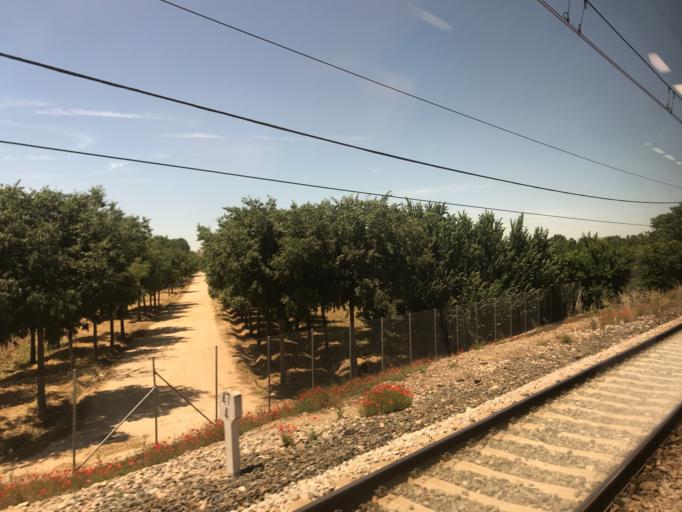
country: ES
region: Madrid
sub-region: Provincia de Madrid
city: Aranjuez
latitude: 40.0425
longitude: -3.6211
